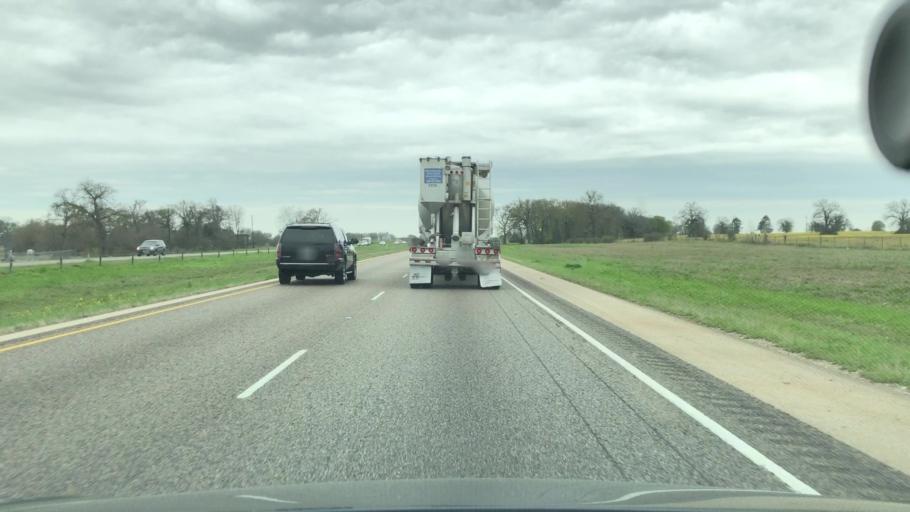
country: US
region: Texas
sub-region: Madison County
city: Madisonville
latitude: 31.0620
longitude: -95.9507
